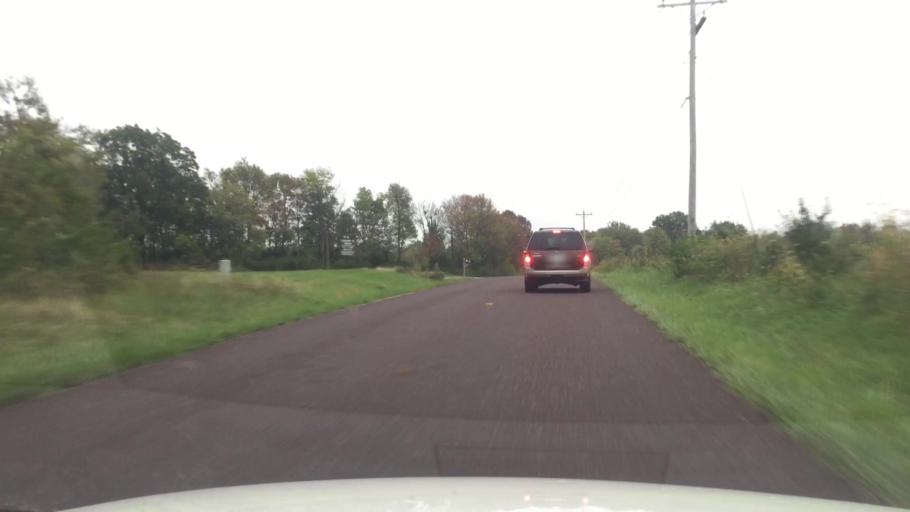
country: US
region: Missouri
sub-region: Boone County
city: Ashland
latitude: 38.8107
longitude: -92.2573
